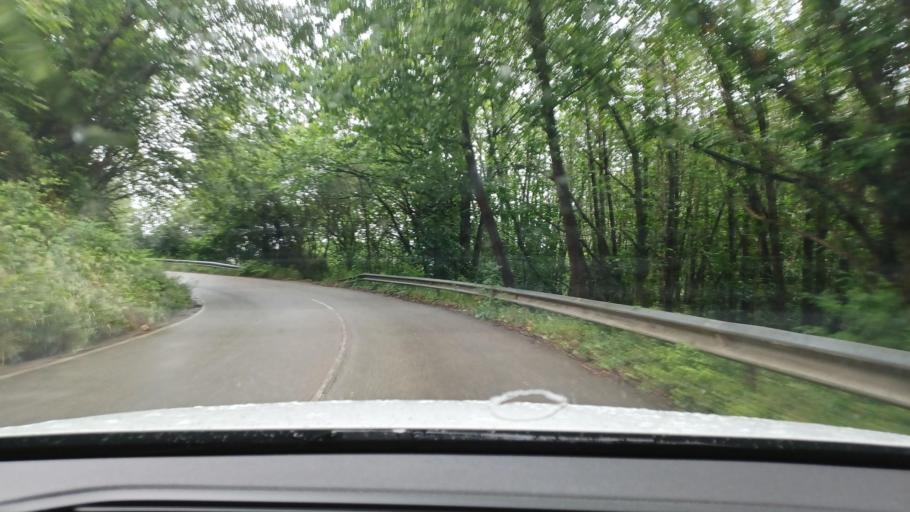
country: ES
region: Asturias
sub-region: Province of Asturias
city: Castandiello
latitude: 43.3134
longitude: -5.9261
